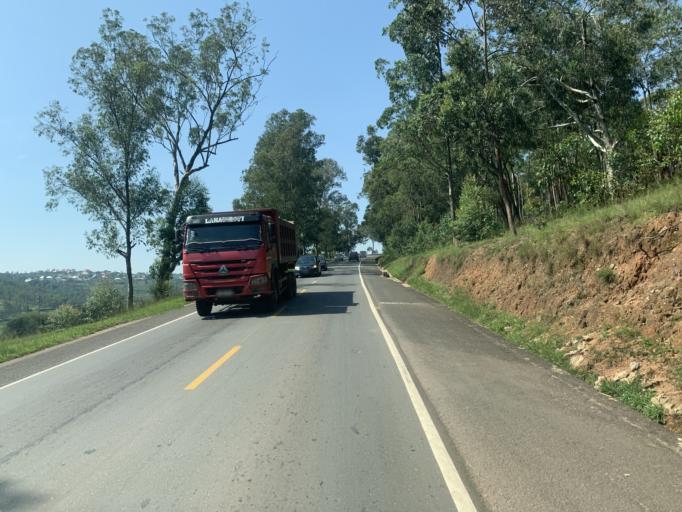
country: RW
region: Kigali
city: Kigali
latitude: -1.9926
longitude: 29.9280
